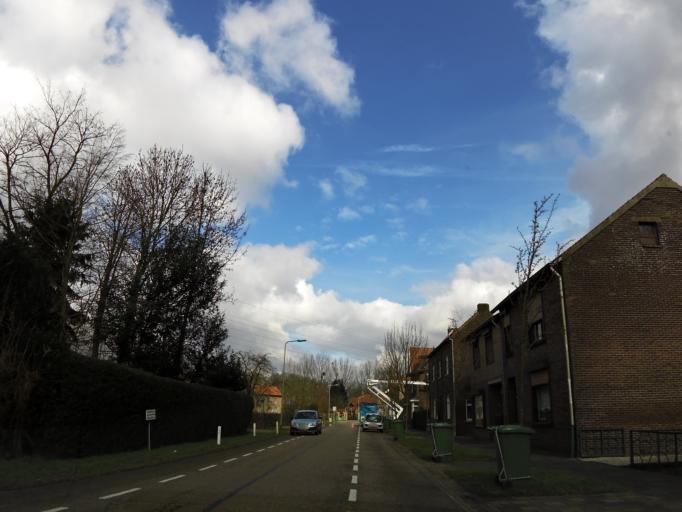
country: NL
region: Limburg
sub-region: Gemeente Meerssen
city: Meerssen
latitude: 50.9194
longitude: 5.7399
